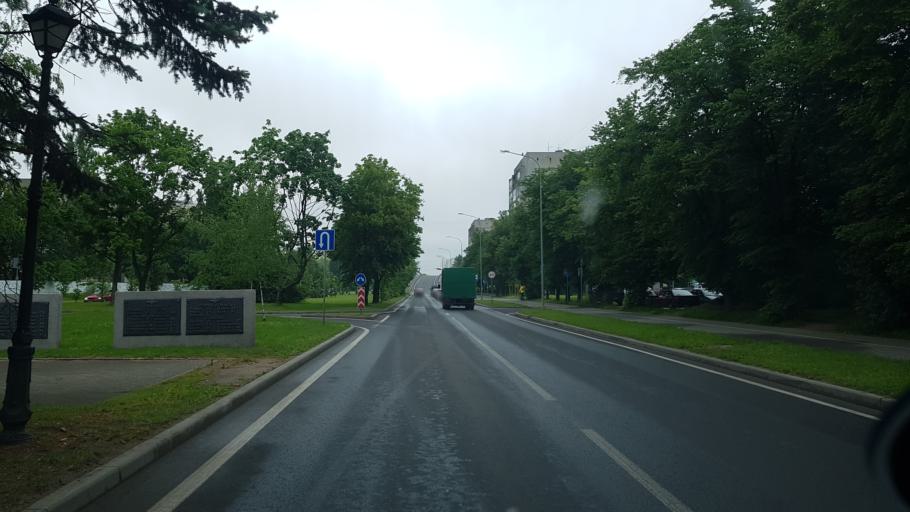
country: RU
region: Kaliningrad
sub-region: Gorod Kaliningrad
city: Kaliningrad
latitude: 54.7310
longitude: 20.4906
